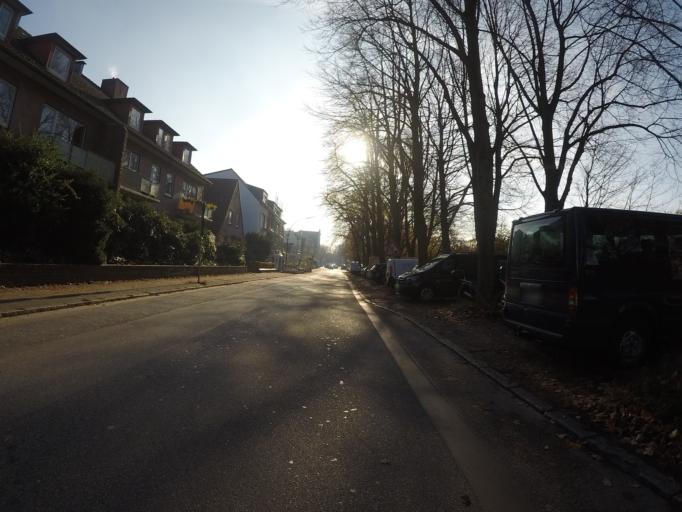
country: DE
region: Hamburg
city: Stellingen
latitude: 53.5942
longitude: 9.9329
